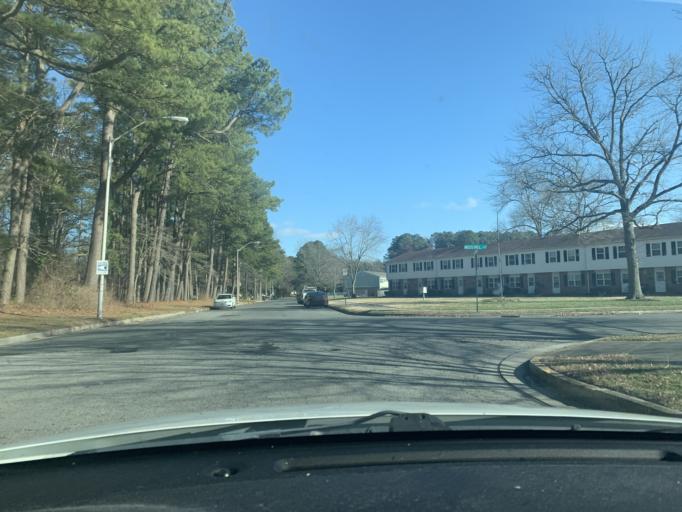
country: US
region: Maryland
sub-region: Wicomico County
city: Salisbury
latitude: 38.3816
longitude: -75.5731
